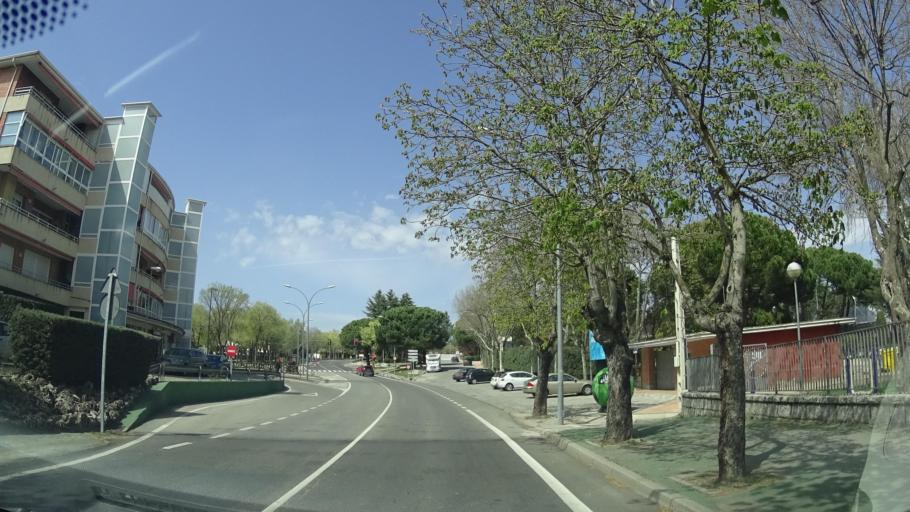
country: ES
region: Madrid
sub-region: Provincia de Madrid
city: Colmenar Viejo
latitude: 40.6720
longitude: -3.7696
